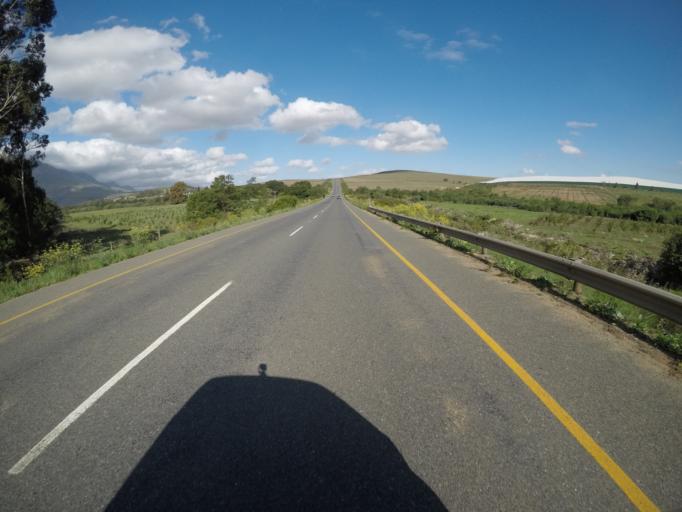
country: ZA
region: Western Cape
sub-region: Overberg District Municipality
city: Swellendam
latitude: -33.9628
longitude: 20.2431
